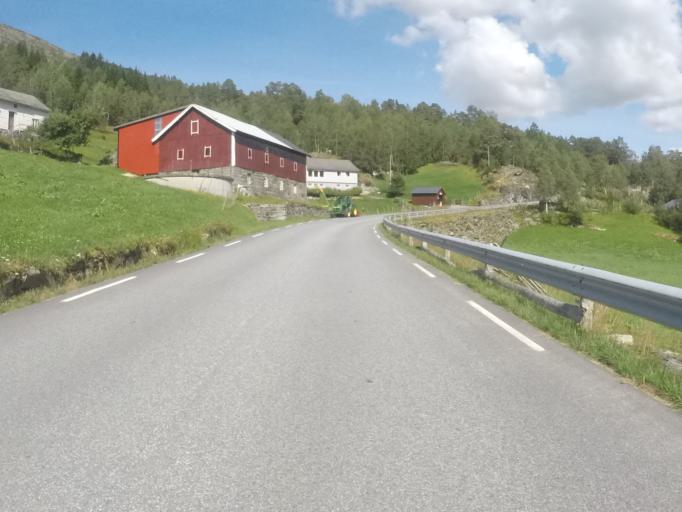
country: NO
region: Sogn og Fjordane
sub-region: Hoyanger
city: Hoyanger
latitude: 61.3214
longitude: 6.2543
